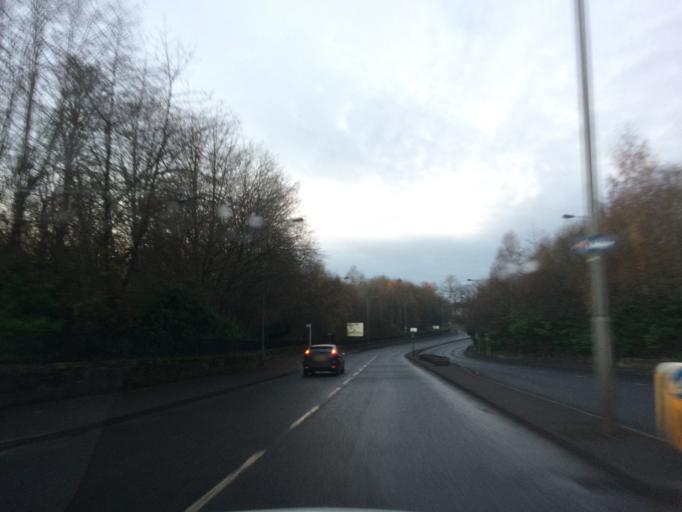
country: GB
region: Scotland
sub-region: East Renfrewshire
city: Giffnock
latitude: 55.8002
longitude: -4.3189
